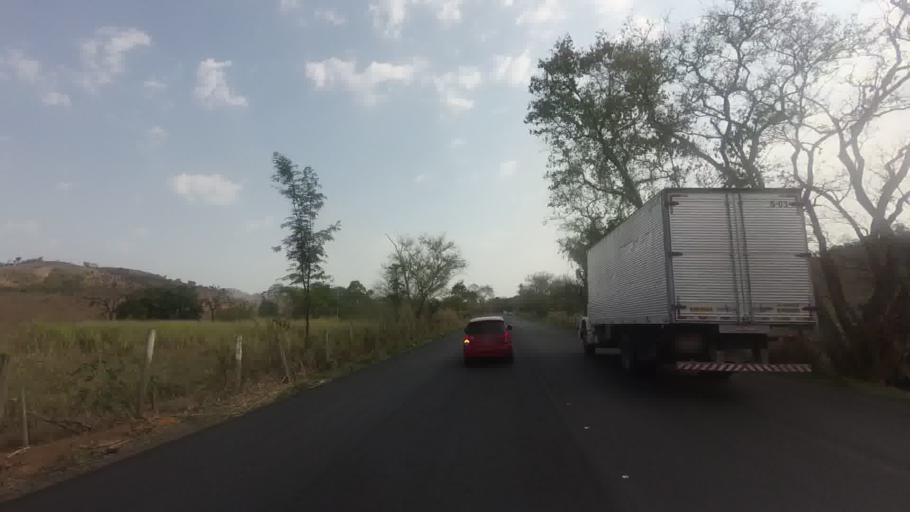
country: BR
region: Rio de Janeiro
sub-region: Bom Jesus Do Itabapoana
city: Bom Jesus do Itabapoana
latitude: -21.1875
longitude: -41.6911
